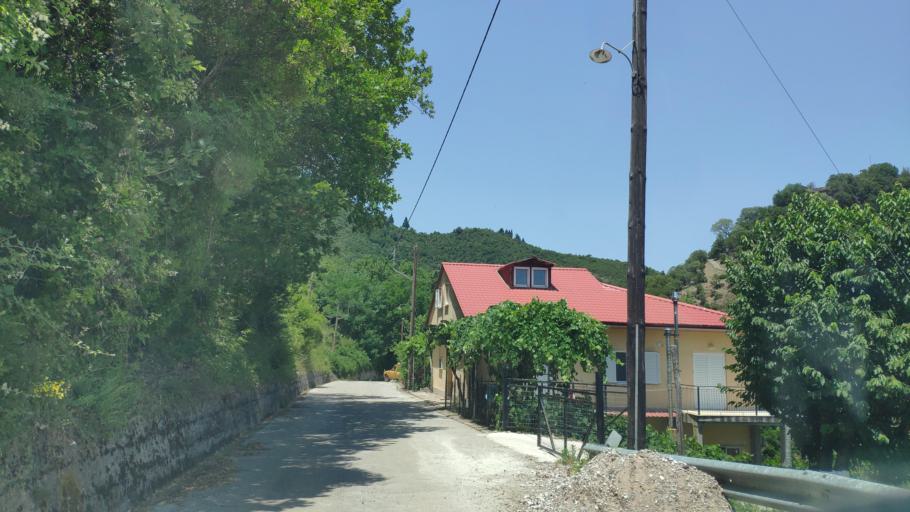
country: GR
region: Epirus
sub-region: Nomos Artas
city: Ano Kalentini
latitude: 39.2027
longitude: 21.3406
